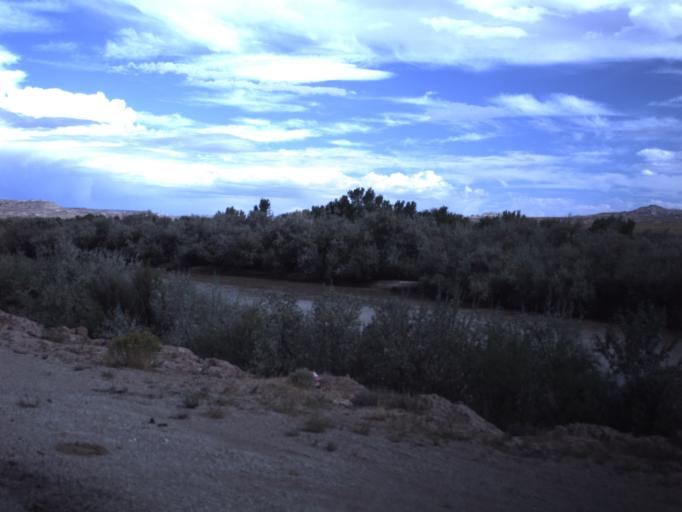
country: US
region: Utah
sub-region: San Juan County
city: Blanding
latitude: 37.2574
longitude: -109.2869
